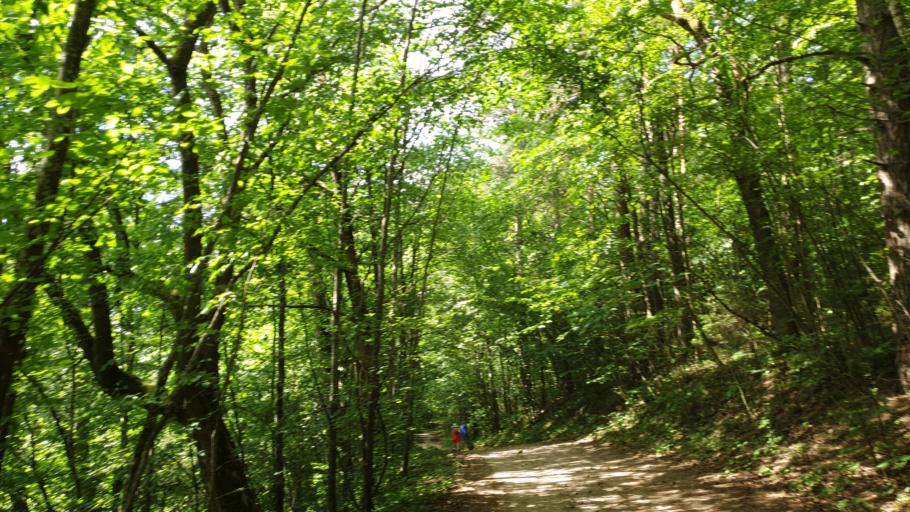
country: LT
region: Vilnius County
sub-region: Vilnius
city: Fabijoniskes
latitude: 54.7899
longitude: 25.3117
